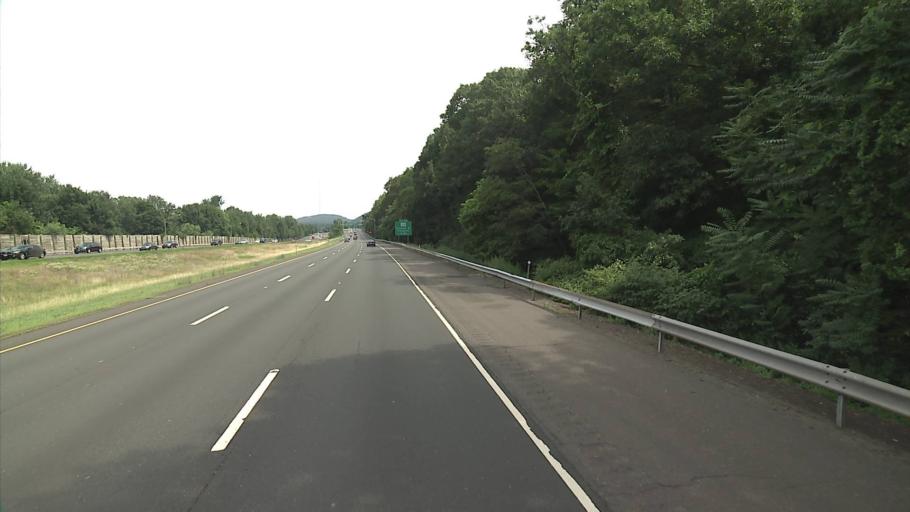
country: US
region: Connecticut
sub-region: Hartford County
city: Plainville
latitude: 41.6614
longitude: -72.8482
